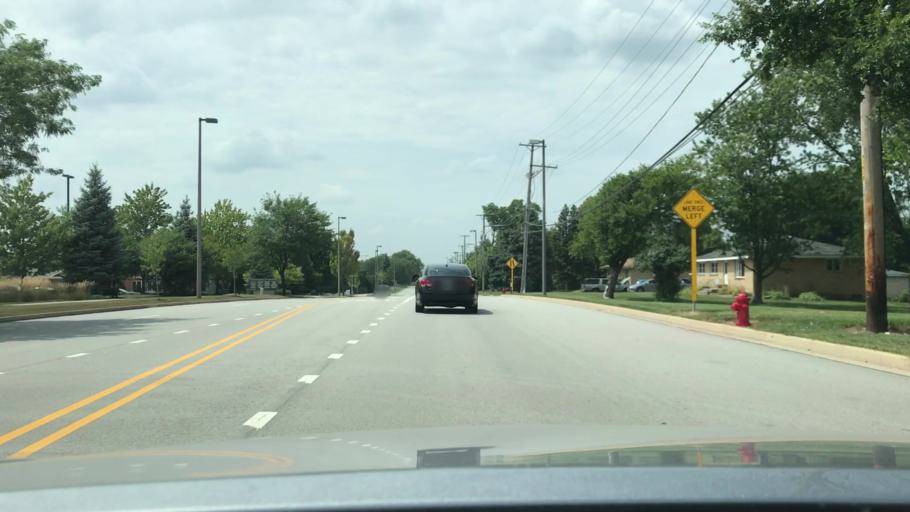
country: US
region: Illinois
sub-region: DuPage County
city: Woodridge
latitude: 41.7366
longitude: -88.0135
